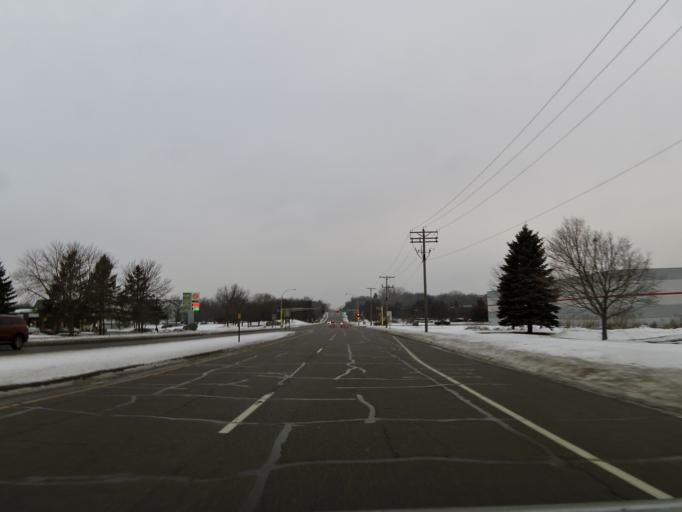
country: US
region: Minnesota
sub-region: Dakota County
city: Mendota Heights
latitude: 44.8480
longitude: -93.1568
